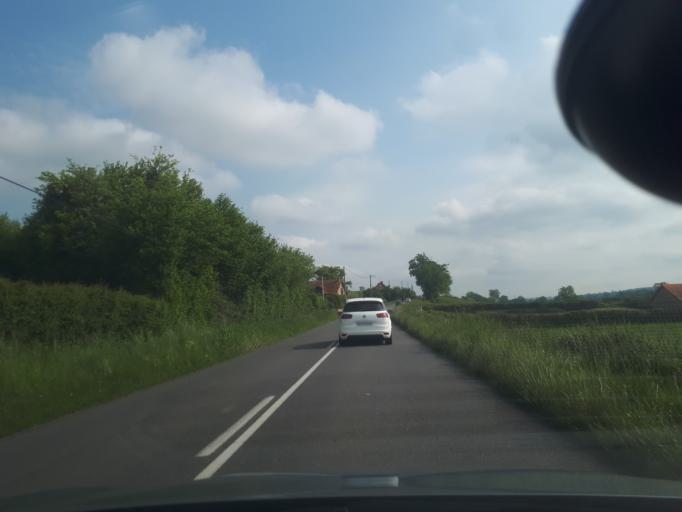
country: FR
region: Auvergne
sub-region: Departement de l'Allier
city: Dompierre-sur-Besbre
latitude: 46.4016
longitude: 3.5991
